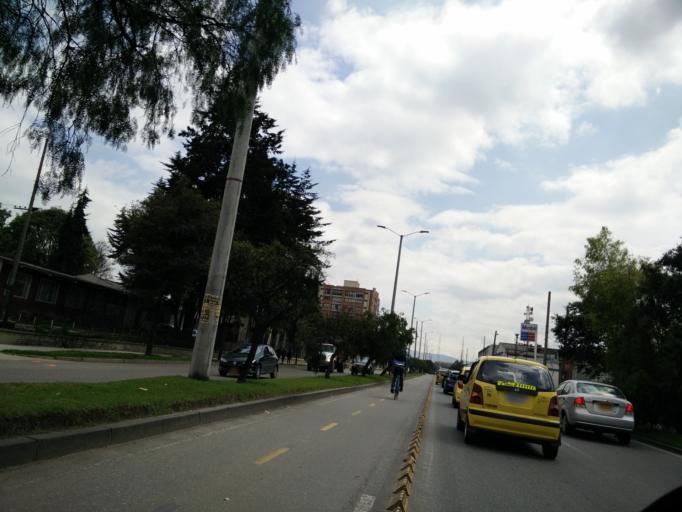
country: CO
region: Bogota D.C.
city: Bogota
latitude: 4.6326
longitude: -74.1030
